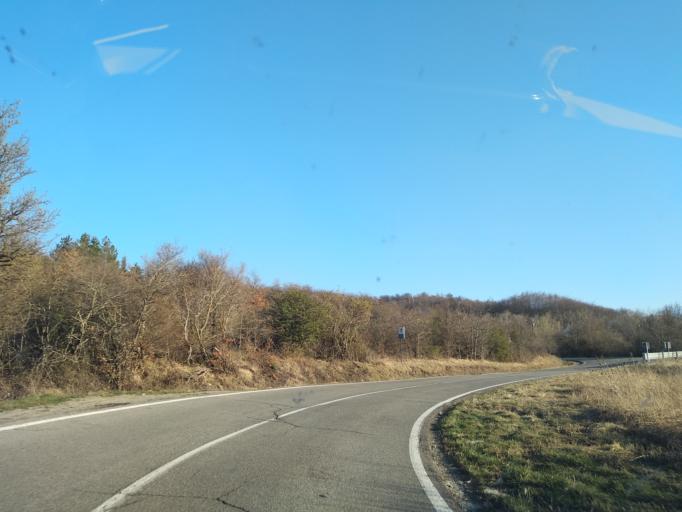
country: IT
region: Emilia-Romagna
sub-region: Provincia di Reggio Emilia
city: Busana
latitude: 44.4083
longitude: 10.3256
